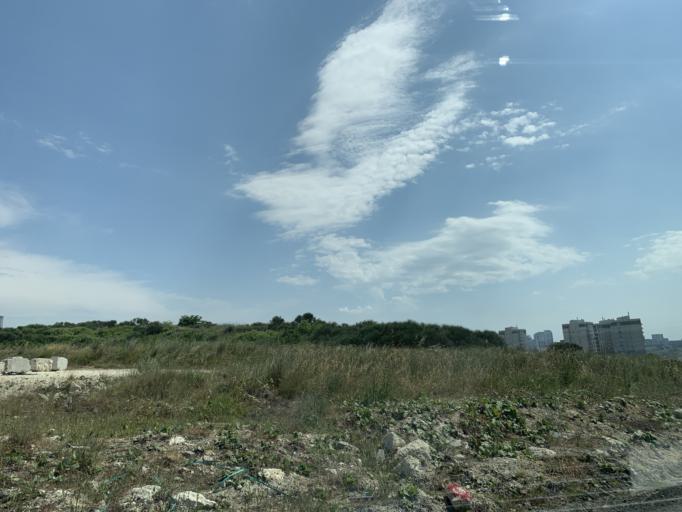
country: TR
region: Istanbul
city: Esenyurt
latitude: 41.0876
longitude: 28.6915
